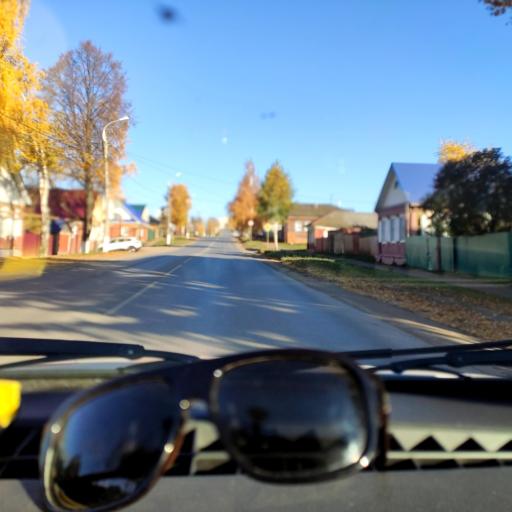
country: RU
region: Bashkortostan
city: Blagoveshchensk
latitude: 55.0383
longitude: 55.9631
